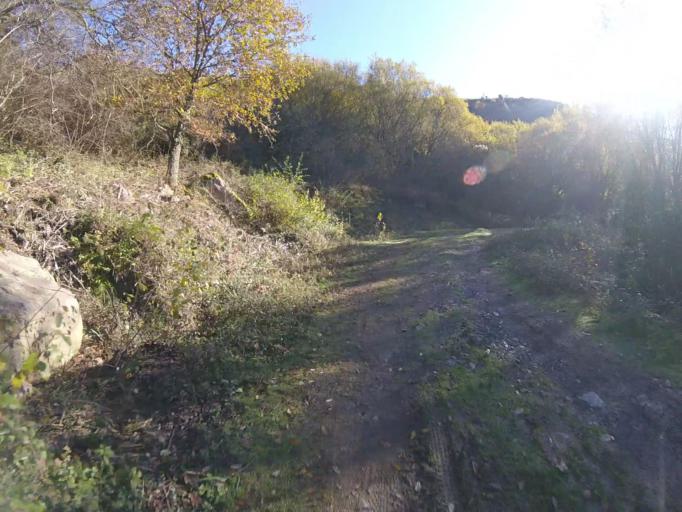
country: FR
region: Aquitaine
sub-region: Departement des Pyrenees-Atlantiques
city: Urrugne
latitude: 43.3298
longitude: -1.7307
